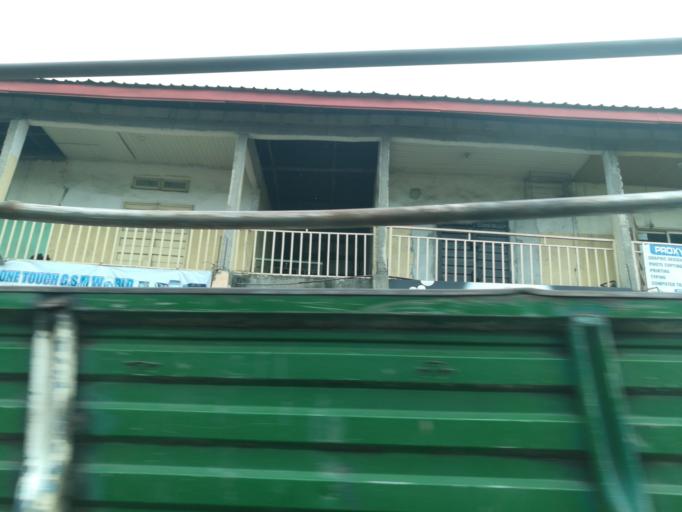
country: NG
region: Rivers
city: Port Harcourt
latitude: 4.8067
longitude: 6.9883
